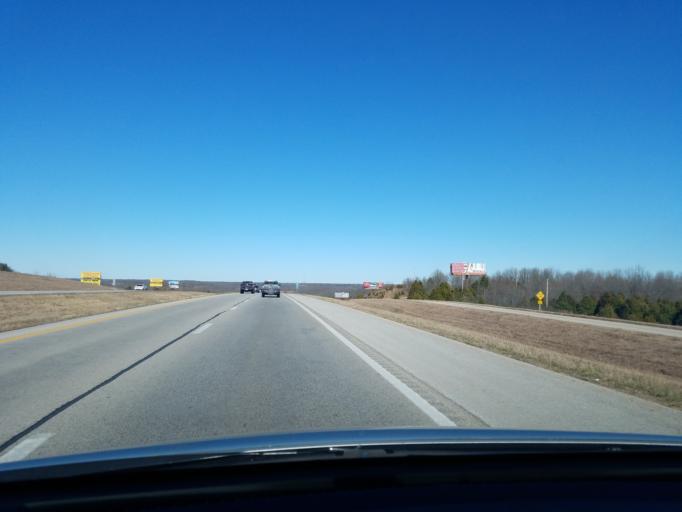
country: US
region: Missouri
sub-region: Taney County
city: Merriam Woods
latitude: 36.8092
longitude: -93.2252
